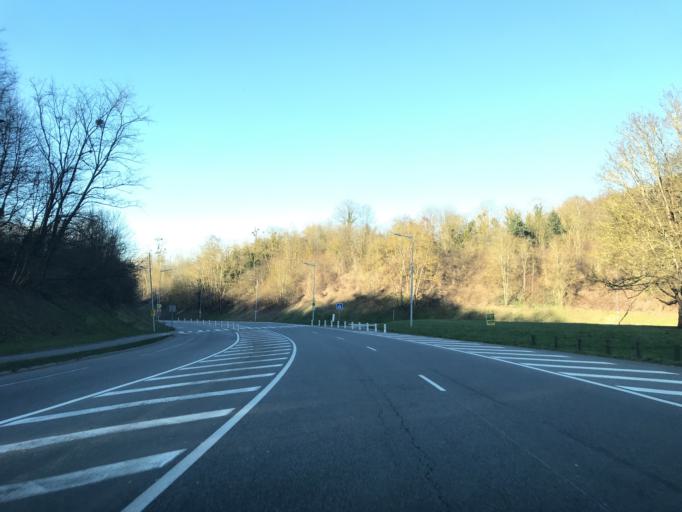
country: FR
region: Haute-Normandie
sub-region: Departement de l'Eure
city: Evreux
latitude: 49.0148
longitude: 1.1443
